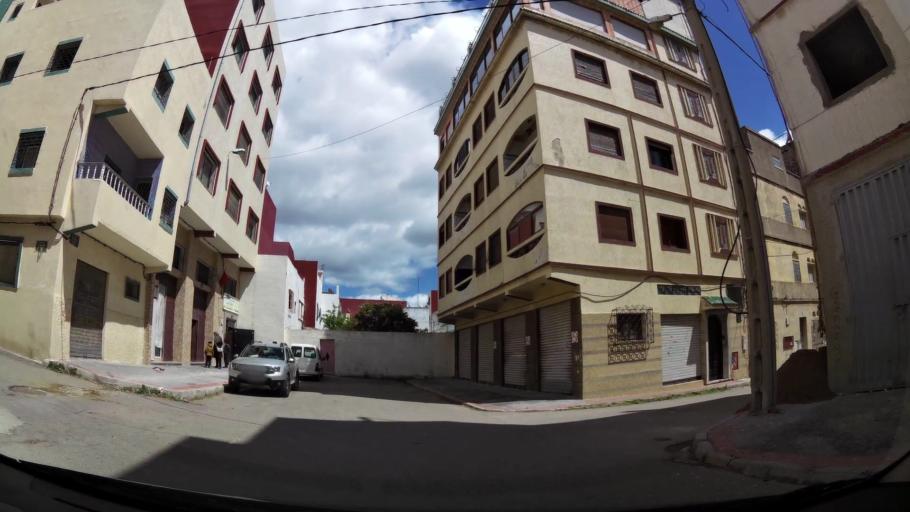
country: MA
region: Tanger-Tetouan
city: Tetouan
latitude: 35.5759
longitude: -5.3464
